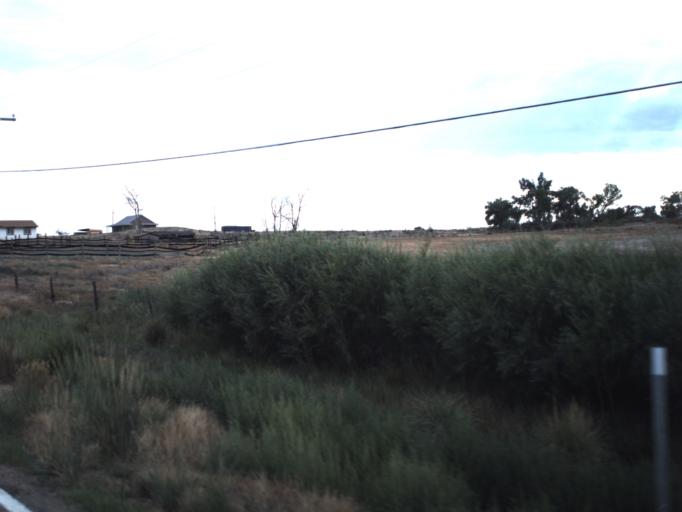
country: US
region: Utah
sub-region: Emery County
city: Huntington
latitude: 39.3928
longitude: -110.8525
